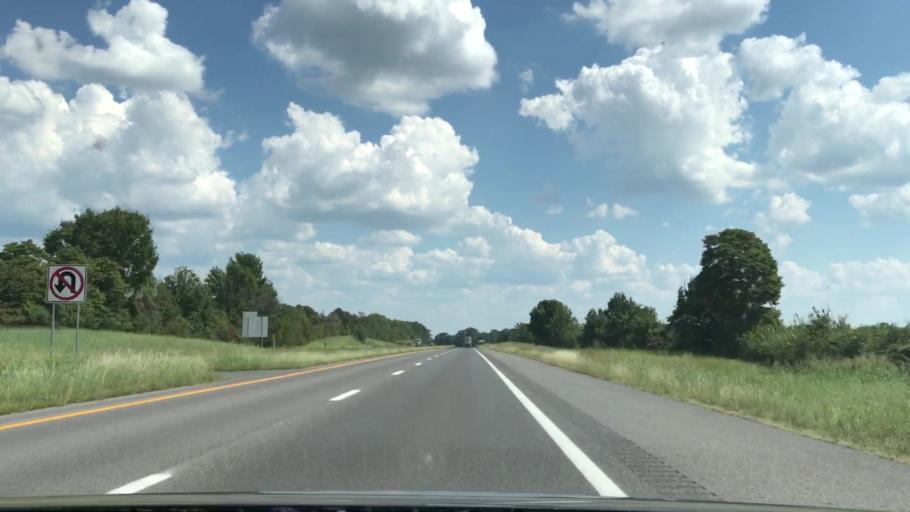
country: US
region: Kentucky
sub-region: Lyon County
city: Eddyville
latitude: 37.1079
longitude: -87.9973
